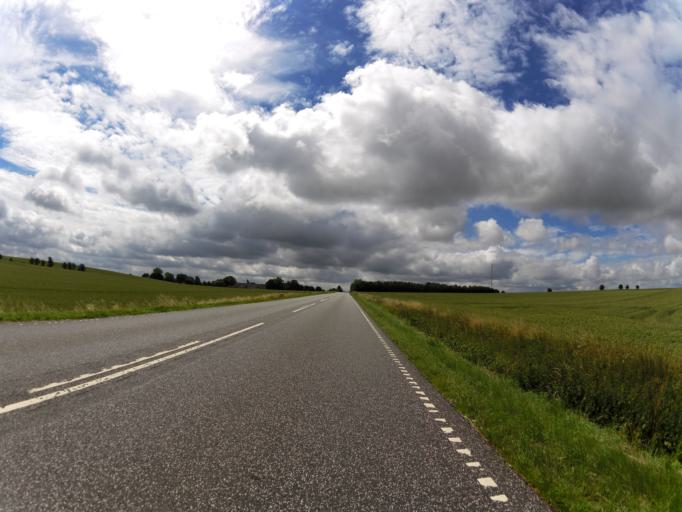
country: DK
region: North Denmark
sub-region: Mariagerfjord Kommune
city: Hadsund
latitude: 56.6158
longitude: 10.1532
